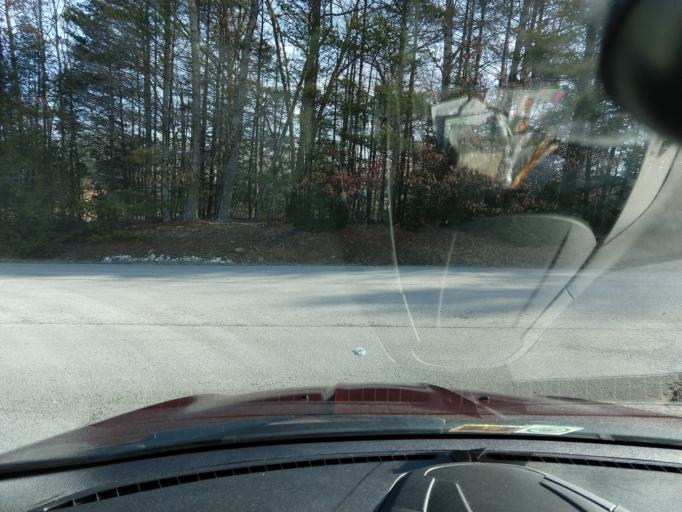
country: US
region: West Virginia
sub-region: Pocahontas County
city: Marlinton
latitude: 38.2011
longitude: -80.1110
